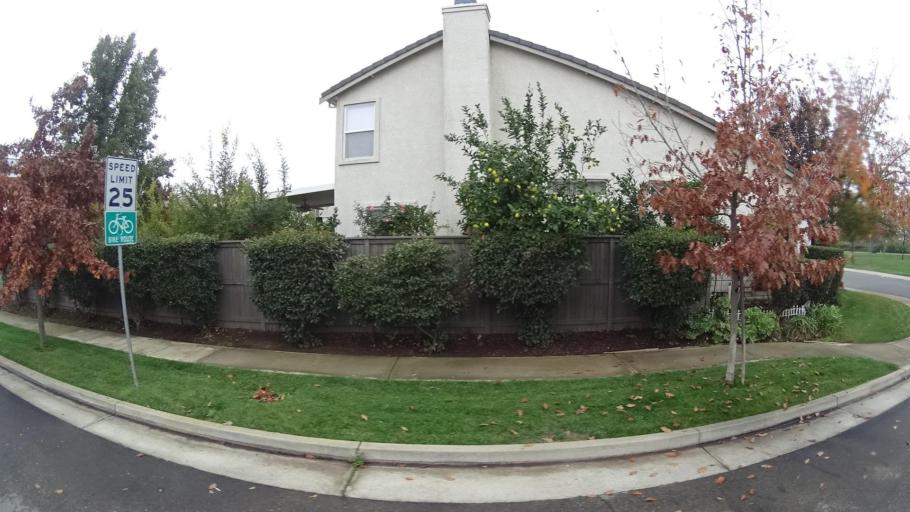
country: US
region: California
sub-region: Sacramento County
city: Elk Grove
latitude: 38.4081
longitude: -121.3480
